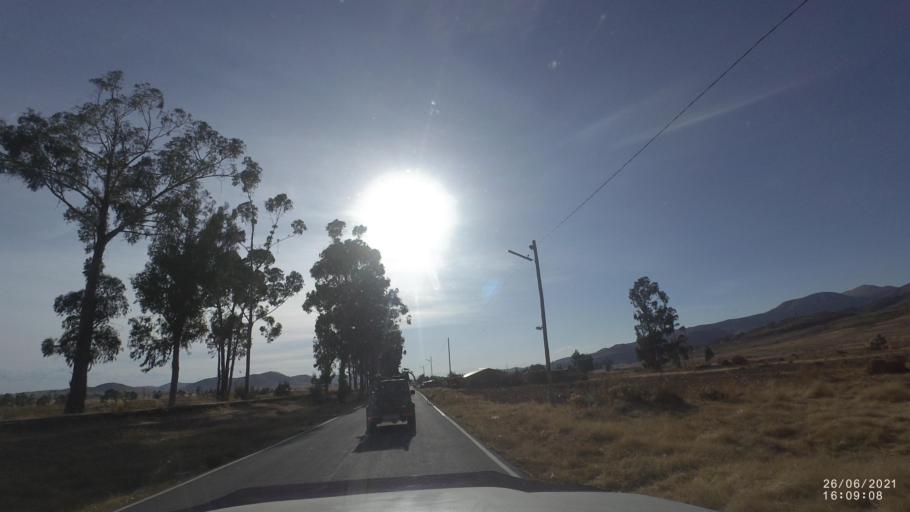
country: BO
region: Cochabamba
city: Arani
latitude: -17.8155
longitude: -65.7821
